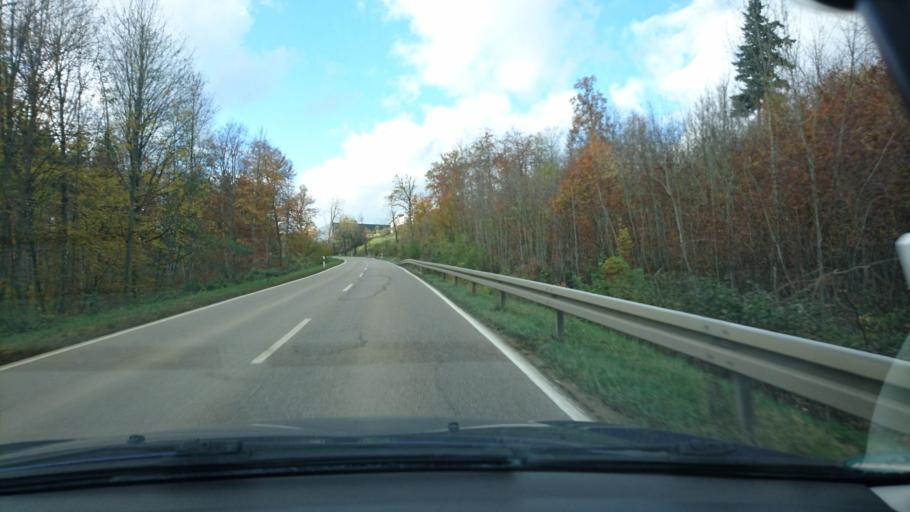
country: DE
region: Baden-Wuerttemberg
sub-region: Regierungsbezirk Stuttgart
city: Abtsgmund
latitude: 48.8919
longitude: 9.9806
